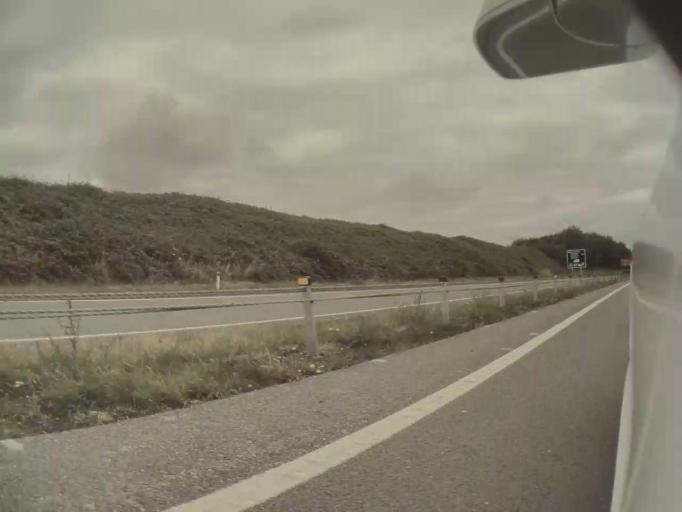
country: GB
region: Wales
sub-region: Anglesey
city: Valley
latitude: 53.2818
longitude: -4.5729
